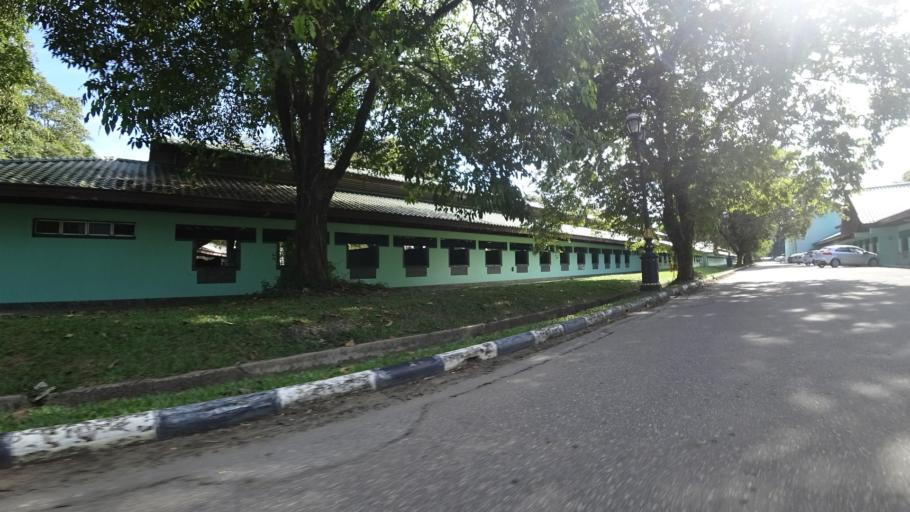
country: BN
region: Brunei and Muara
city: Bandar Seri Begawan
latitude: 4.9499
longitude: 114.8331
